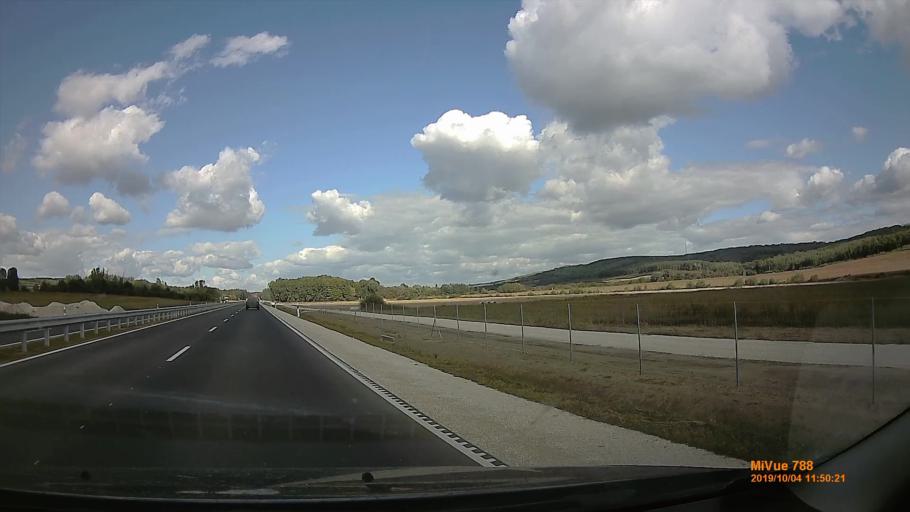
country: HU
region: Somogy
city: Karad
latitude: 46.6840
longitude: 17.7747
